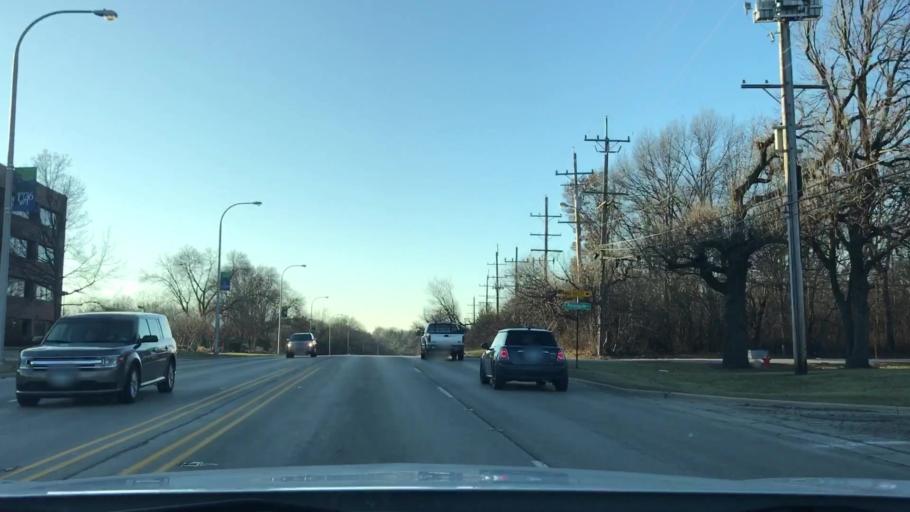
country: US
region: Illinois
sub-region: Kane County
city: Elgin
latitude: 42.0585
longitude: -88.2970
